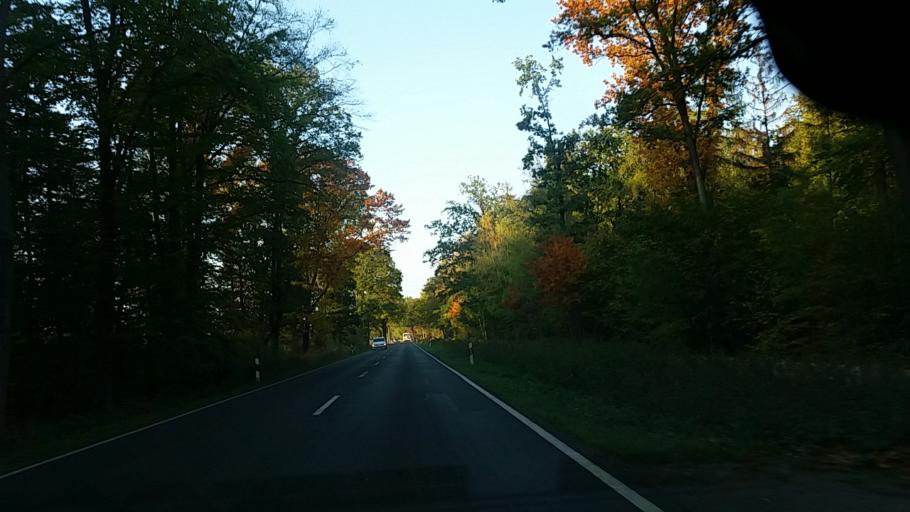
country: DE
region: Lower Saxony
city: Wolfsburg
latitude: 52.3776
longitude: 10.7429
